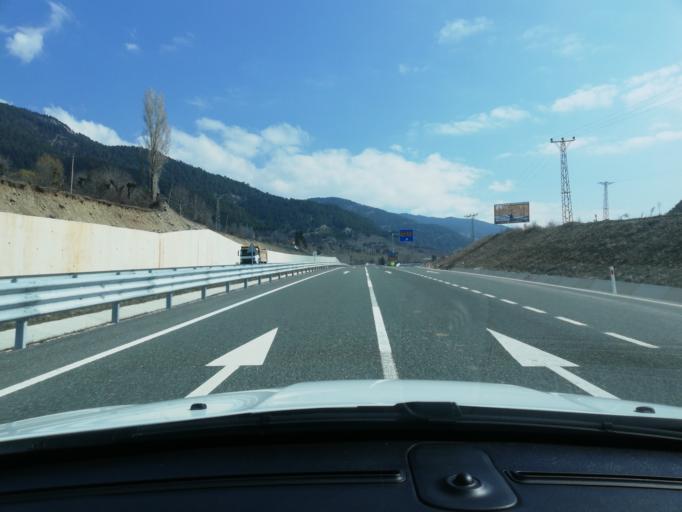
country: TR
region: Cankiri
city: Ilgaz
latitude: 41.0242
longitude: 33.7164
